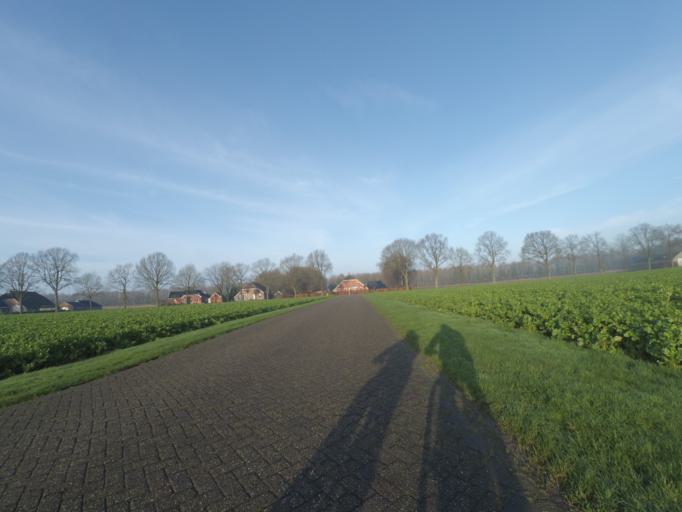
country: NL
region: Drenthe
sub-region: Gemeente Borger-Odoorn
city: Borger
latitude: 52.9067
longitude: 6.7724
